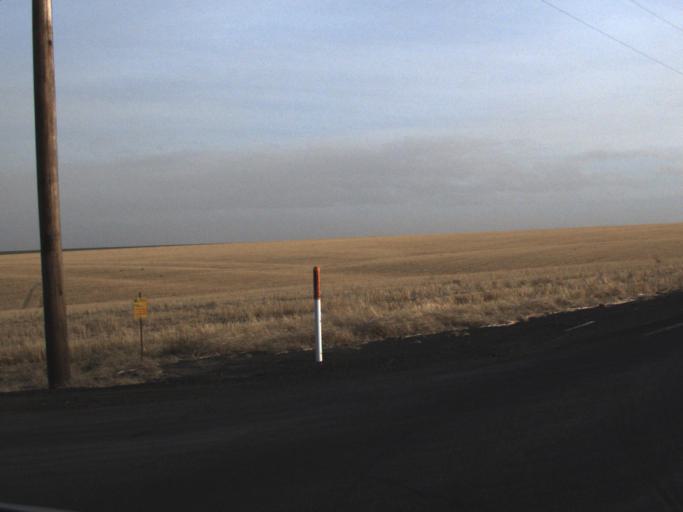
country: US
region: Washington
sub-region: Adams County
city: Ritzville
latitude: 47.2065
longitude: -118.6865
